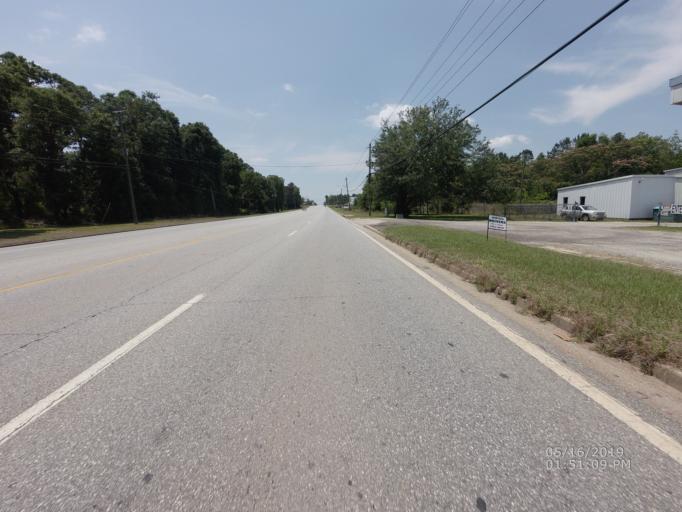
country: US
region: Georgia
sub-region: Dougherty County
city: Albany
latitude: 31.5491
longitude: -84.2015
